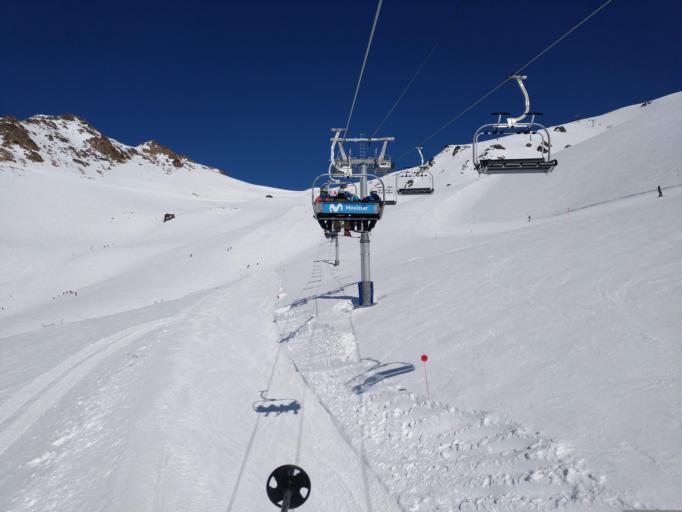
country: AR
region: Rio Negro
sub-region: Departamento de Bariloche
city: San Carlos de Bariloche
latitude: -41.1688
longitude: -71.4748
